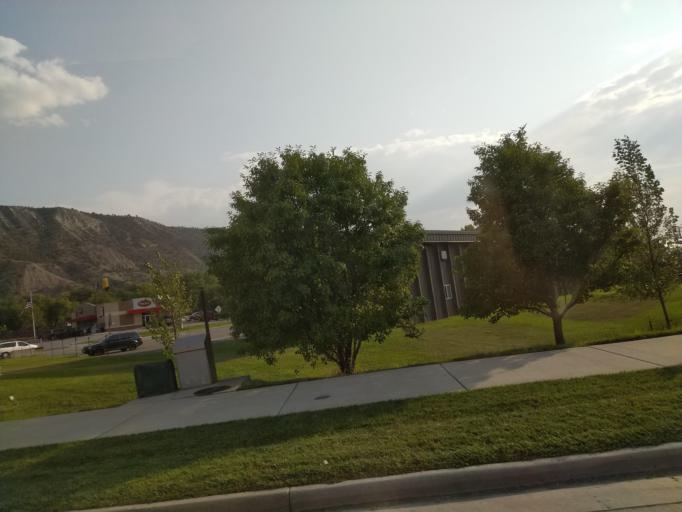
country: US
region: Colorado
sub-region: Garfield County
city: Rifle
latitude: 39.5231
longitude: -107.7773
